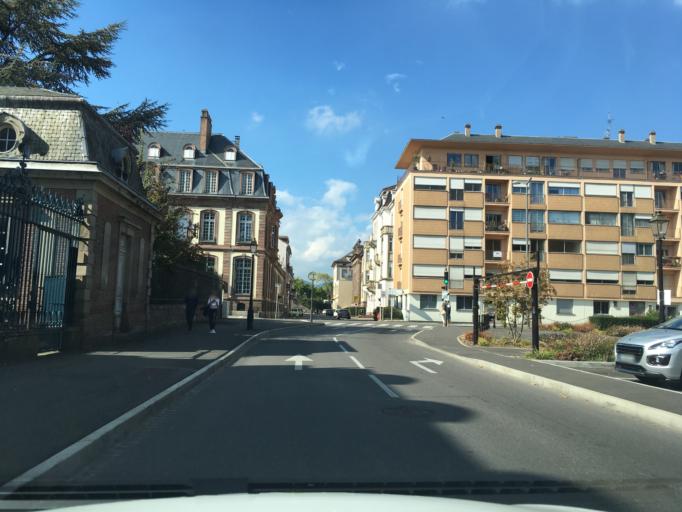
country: FR
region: Alsace
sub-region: Departement du Haut-Rhin
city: Colmar
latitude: 48.0747
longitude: 7.3513
